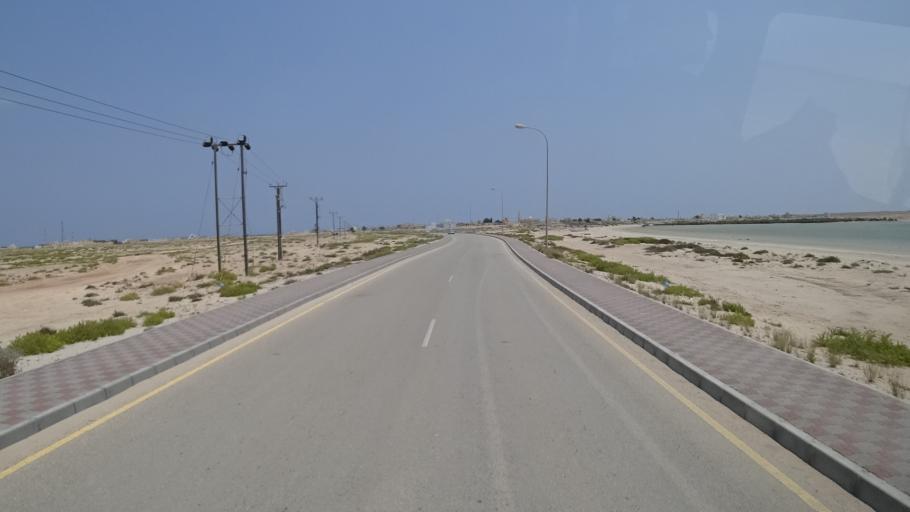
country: OM
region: Ash Sharqiyah
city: Sur
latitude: 22.5283
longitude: 59.7811
